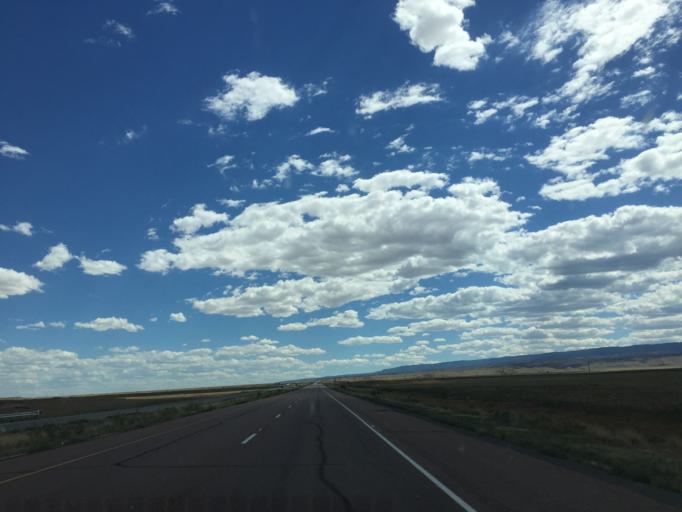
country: US
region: New Mexico
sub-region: McKinley County
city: Navajo
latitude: 36.2319
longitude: -108.7086
